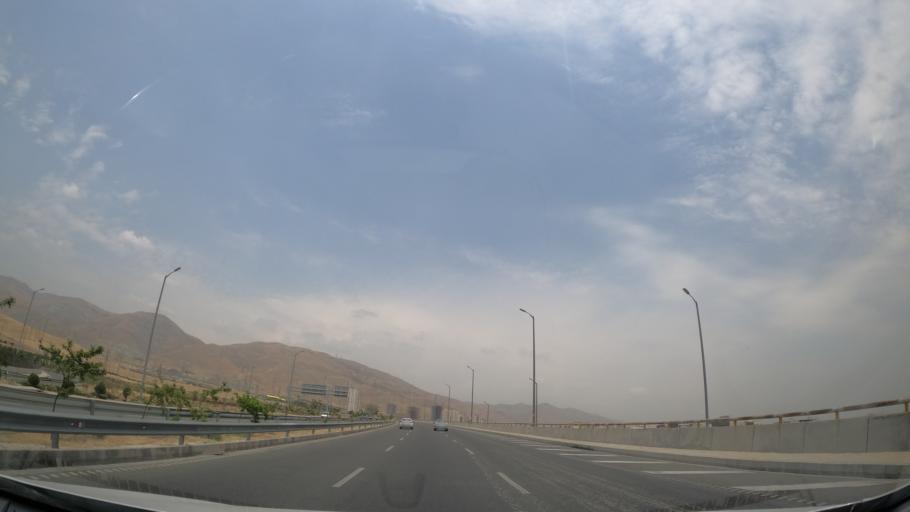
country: IR
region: Tehran
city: Shahr-e Qods
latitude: 35.7401
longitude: 51.1232
